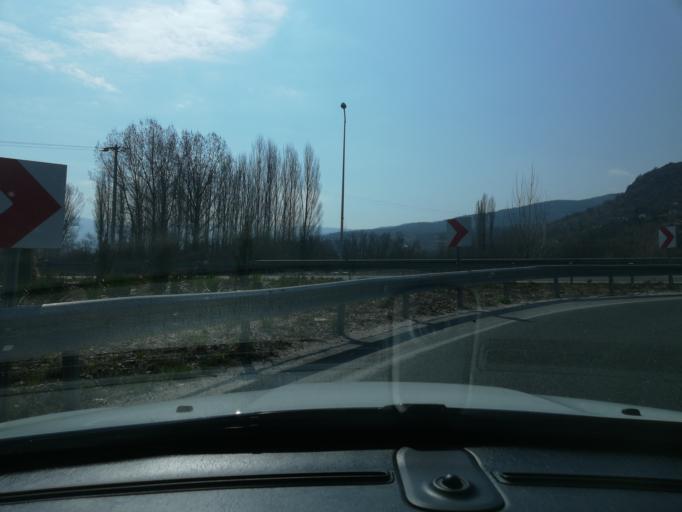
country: TR
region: Cankiri
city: Ilgaz
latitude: 40.9048
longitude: 33.6517
